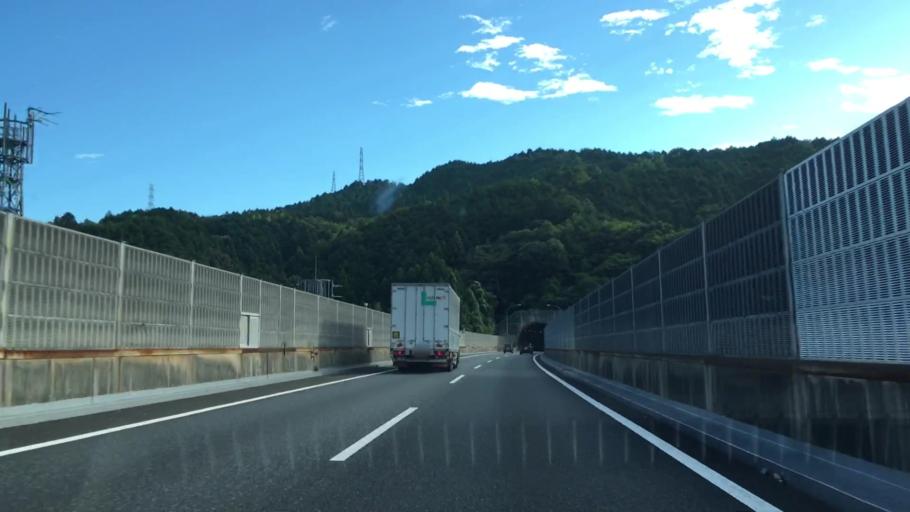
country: JP
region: Yamaguchi
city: Iwakuni
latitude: 34.1578
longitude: 132.1509
